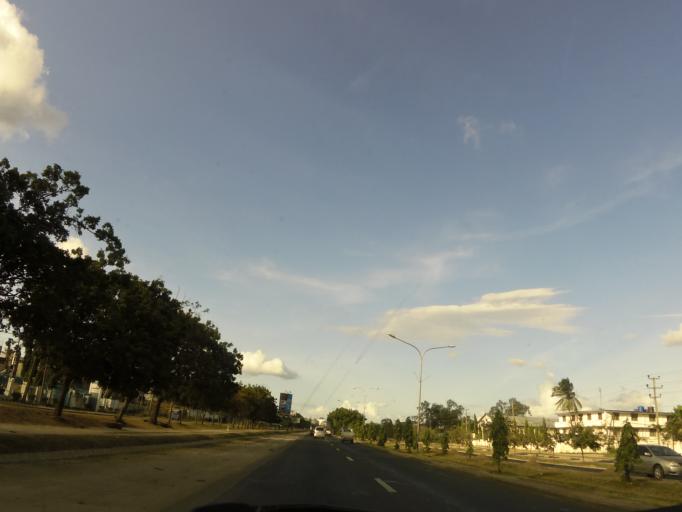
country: TZ
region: Dar es Salaam
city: Dar es Salaam
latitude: -6.8499
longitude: 39.2334
